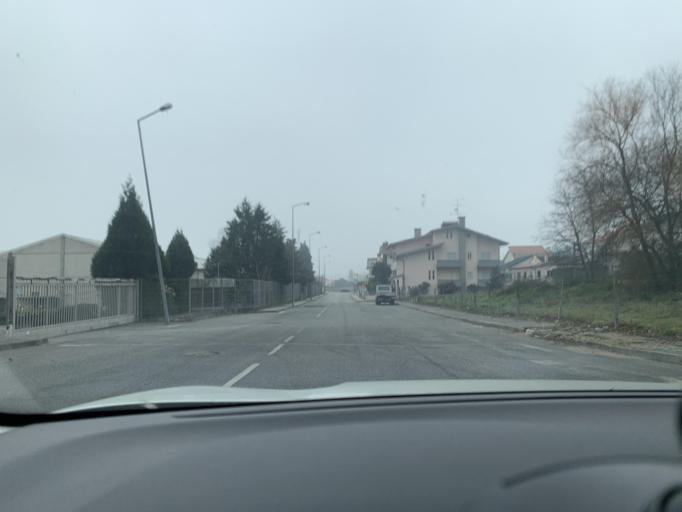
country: PT
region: Viseu
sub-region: Viseu
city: Rio de Loba
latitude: 40.6530
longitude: -7.8855
